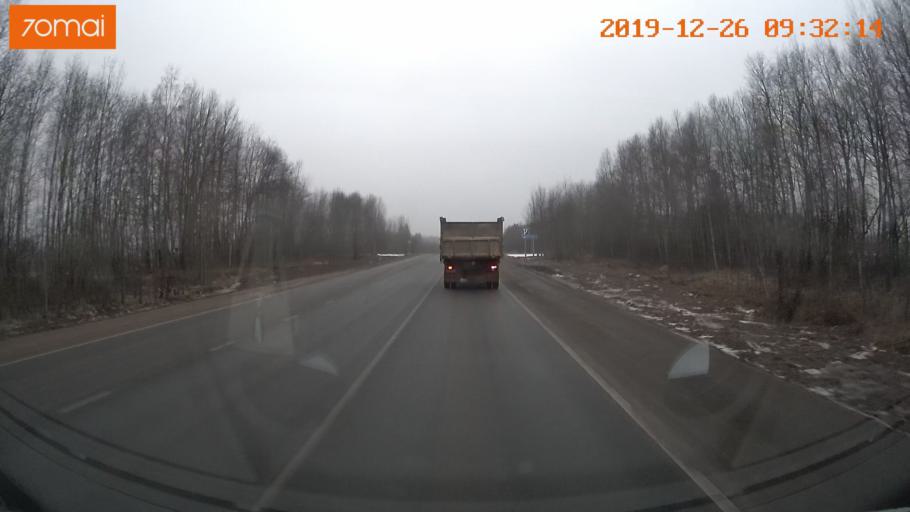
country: RU
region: Vologda
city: Gryazovets
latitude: 59.0757
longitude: 40.1193
